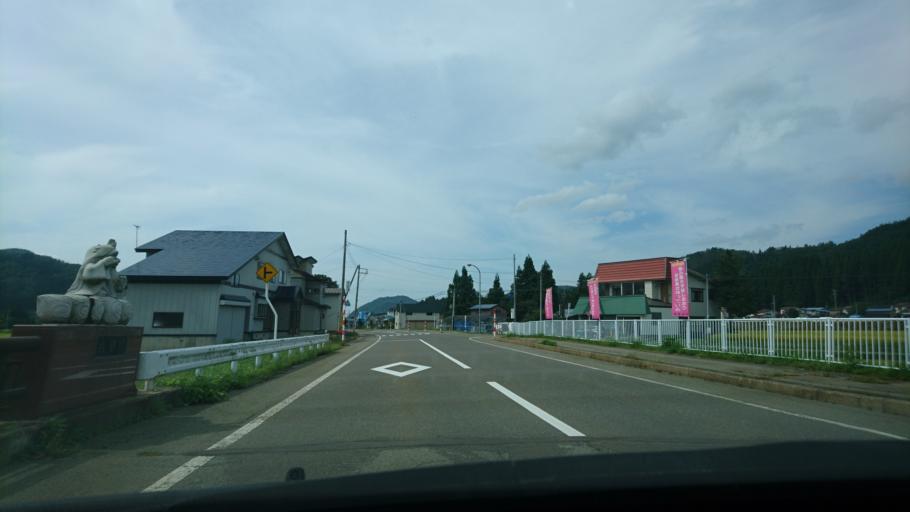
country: JP
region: Akita
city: Yuzawa
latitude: 39.1856
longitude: 140.6349
